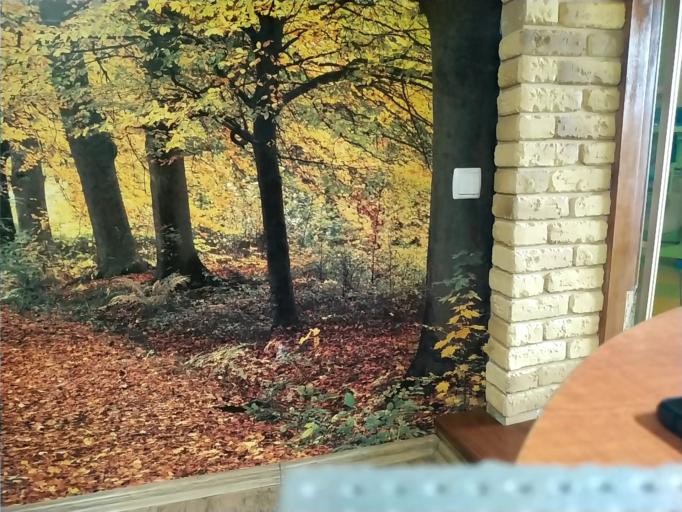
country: RU
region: Tverskaya
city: Kalashnikovo
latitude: 57.2784
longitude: 35.2169
